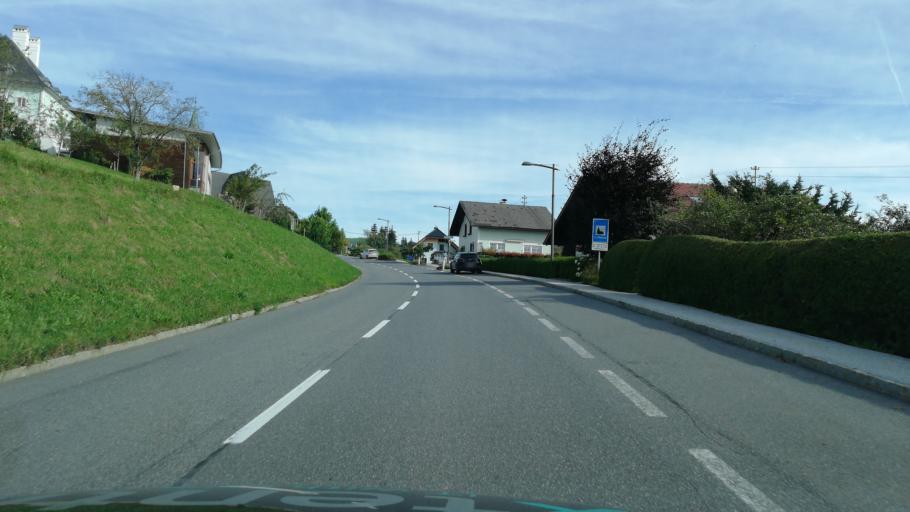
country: AT
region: Upper Austria
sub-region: Politischer Bezirk Steyr-Land
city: Maria Neustift
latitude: 47.9354
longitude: 14.6072
